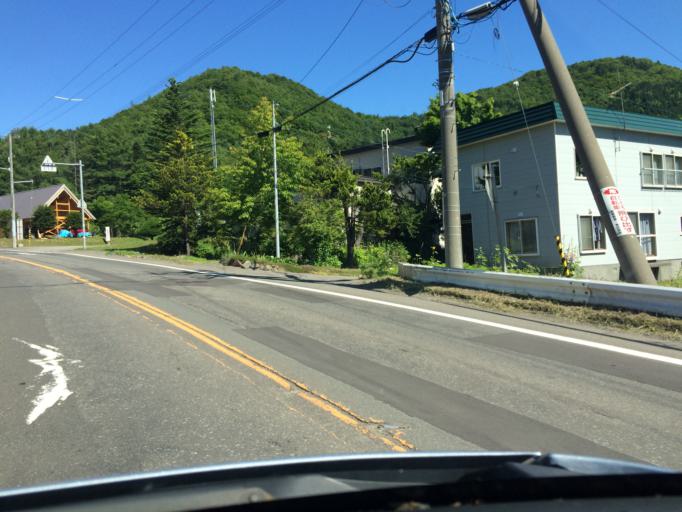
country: JP
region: Hokkaido
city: Sapporo
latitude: 43.0176
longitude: 141.2998
